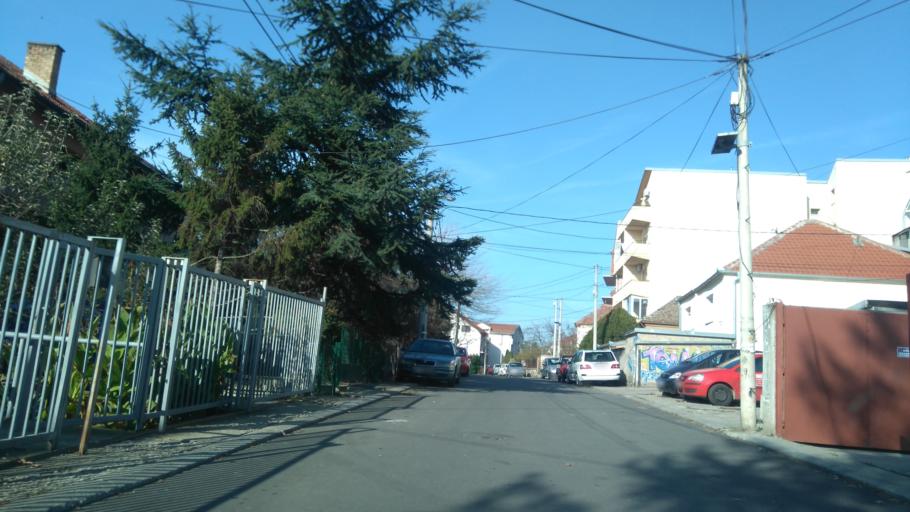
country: RS
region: Central Serbia
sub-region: Belgrade
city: Cukarica
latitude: 44.7572
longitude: 20.4122
